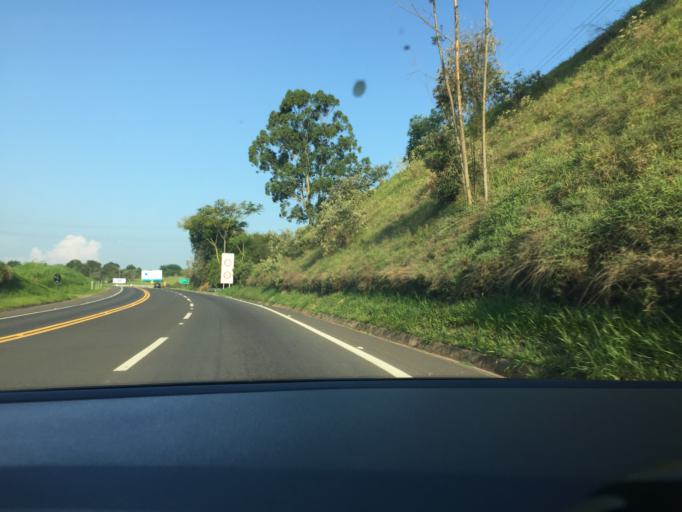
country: BR
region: Sao Paulo
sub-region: Louveira
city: Louveira
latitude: -23.0817
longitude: -46.9129
